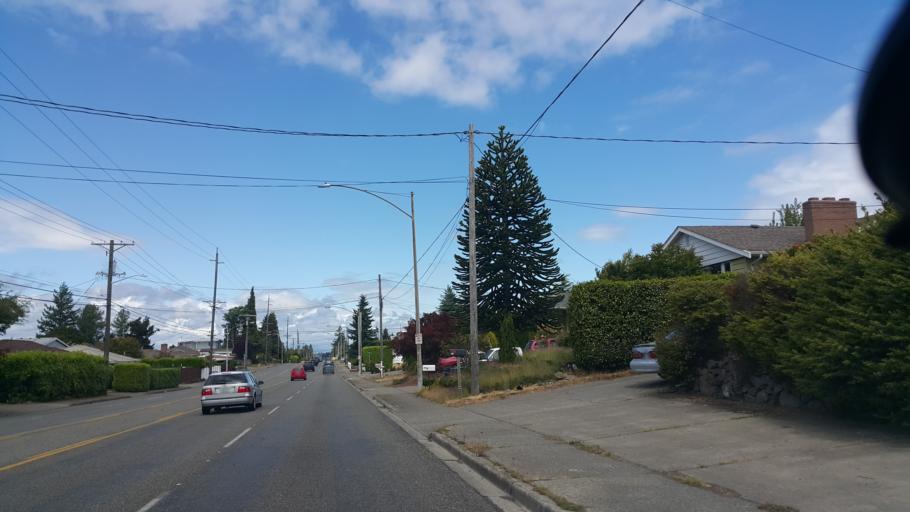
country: US
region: Washington
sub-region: Pierce County
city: University Place
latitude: 47.2457
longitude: -122.5369
